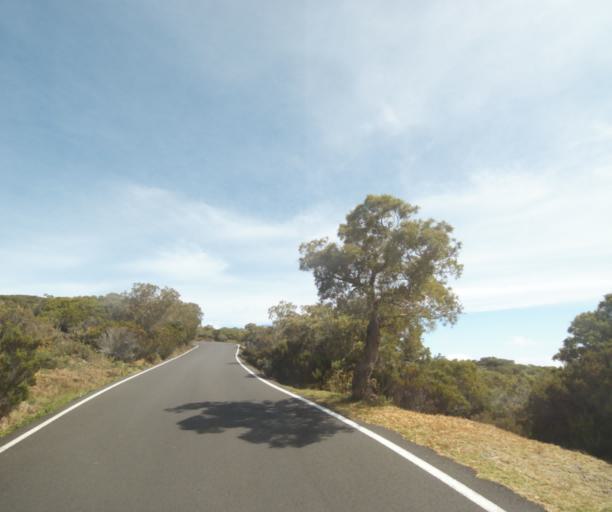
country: RE
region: Reunion
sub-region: Reunion
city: Trois-Bassins
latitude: -21.0714
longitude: 55.3787
